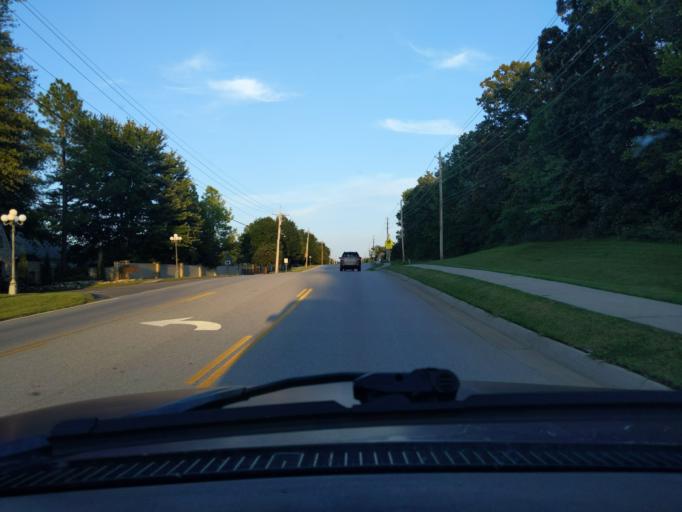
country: US
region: Oklahoma
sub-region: Tulsa County
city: Jenks
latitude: 36.0463
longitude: -95.9177
